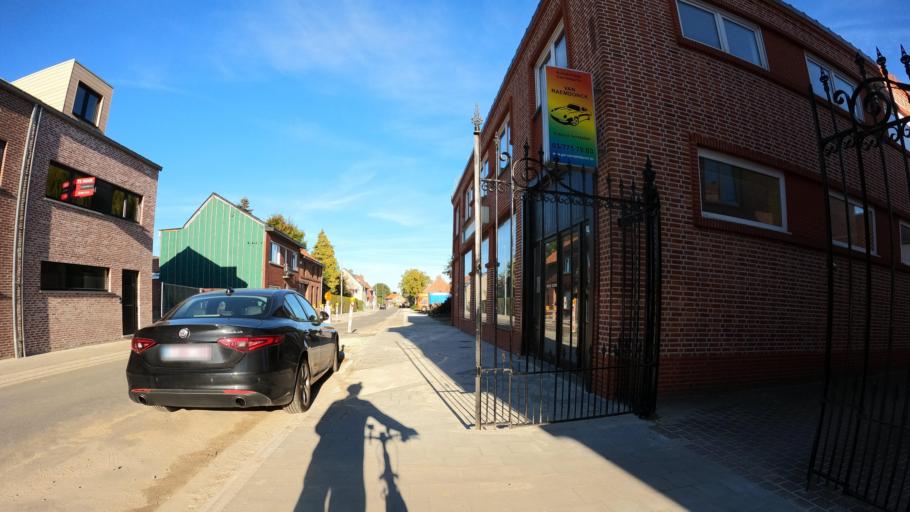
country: BE
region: Flanders
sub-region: Provincie Oost-Vlaanderen
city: Beveren
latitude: 51.1824
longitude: 4.2477
